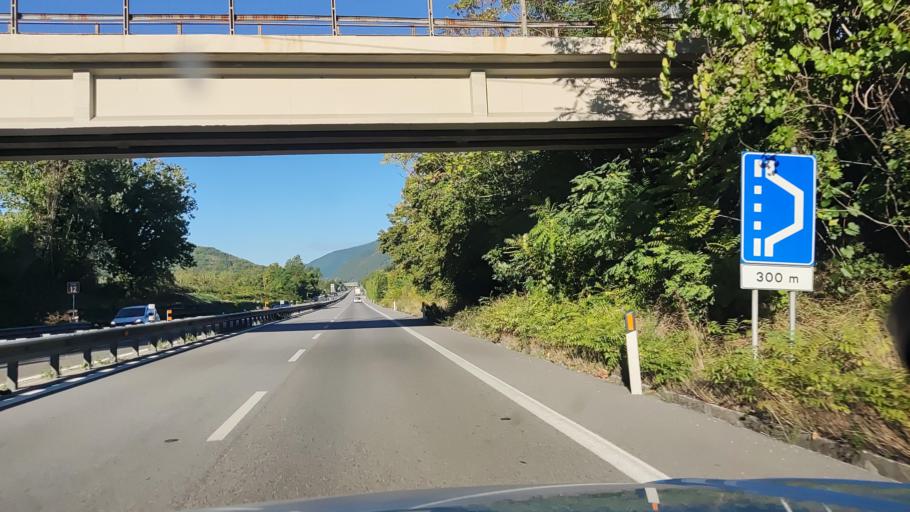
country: IT
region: The Marches
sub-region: Provincia di Pesaro e Urbino
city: Sant'Ippolito
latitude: 43.6875
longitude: 12.8455
